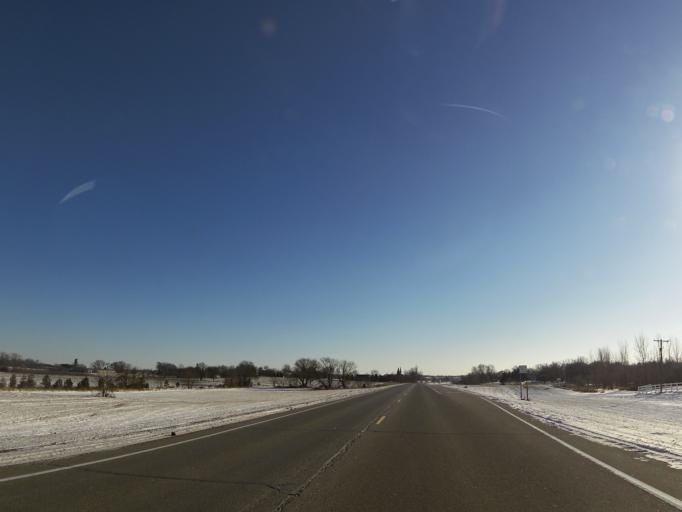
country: US
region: Minnesota
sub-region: Scott County
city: Prior Lake
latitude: 44.6586
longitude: -93.5008
